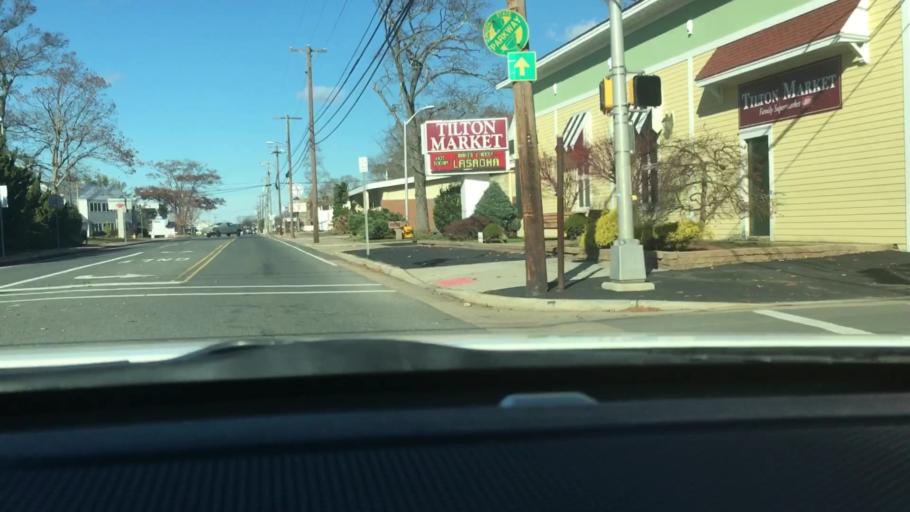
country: US
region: New Jersey
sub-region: Atlantic County
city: Northfield
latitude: 39.3703
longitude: -74.5528
